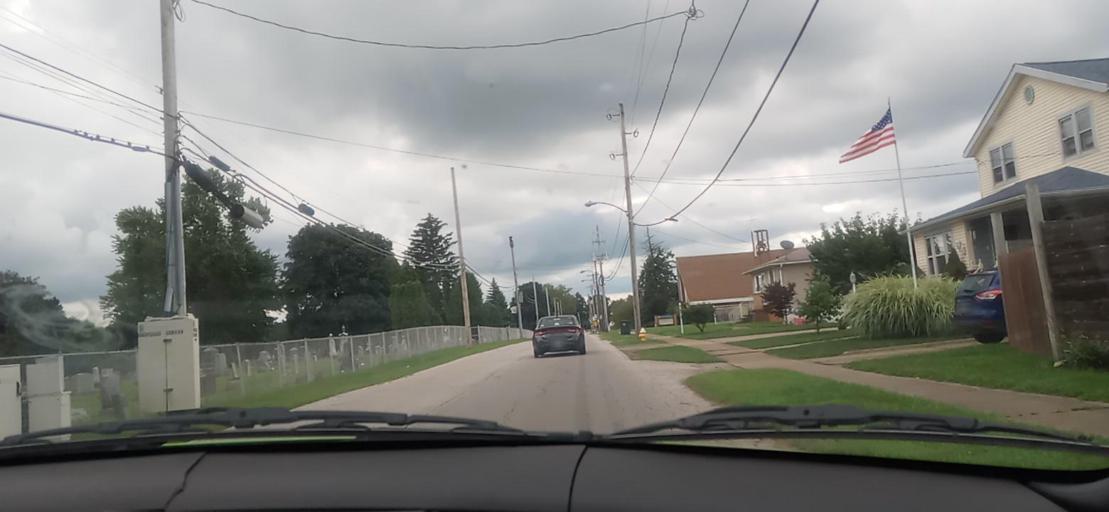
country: US
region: Ohio
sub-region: Summit County
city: Barberton
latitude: 41.0322
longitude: -81.5666
